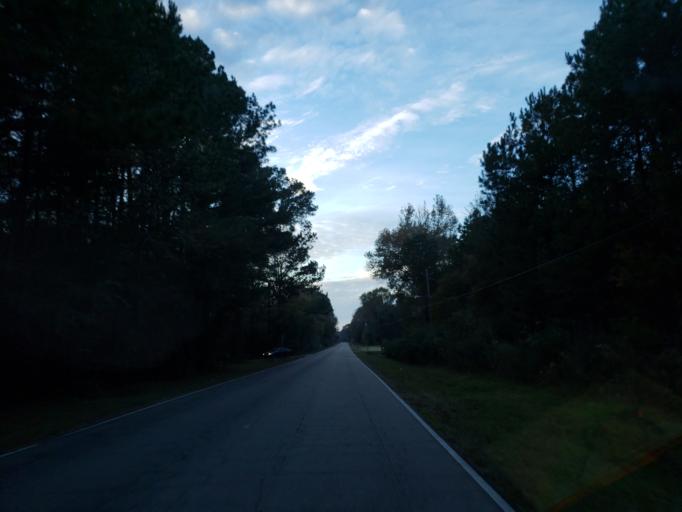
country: US
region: Mississippi
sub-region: Forrest County
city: Hattiesburg
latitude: 31.2830
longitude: -89.2536
